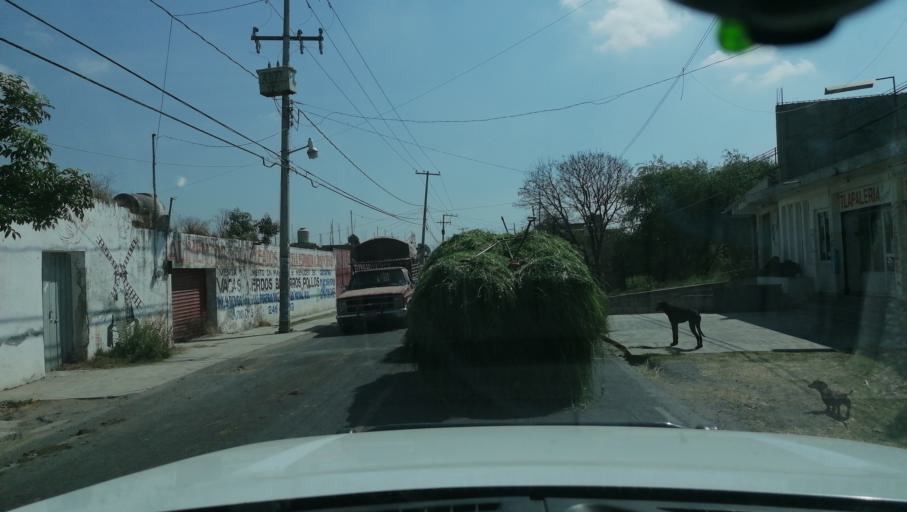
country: MX
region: Tlaxcala
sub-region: Tetlatlahuca
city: Tetlatlahuca
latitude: 19.2314
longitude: -98.2920
